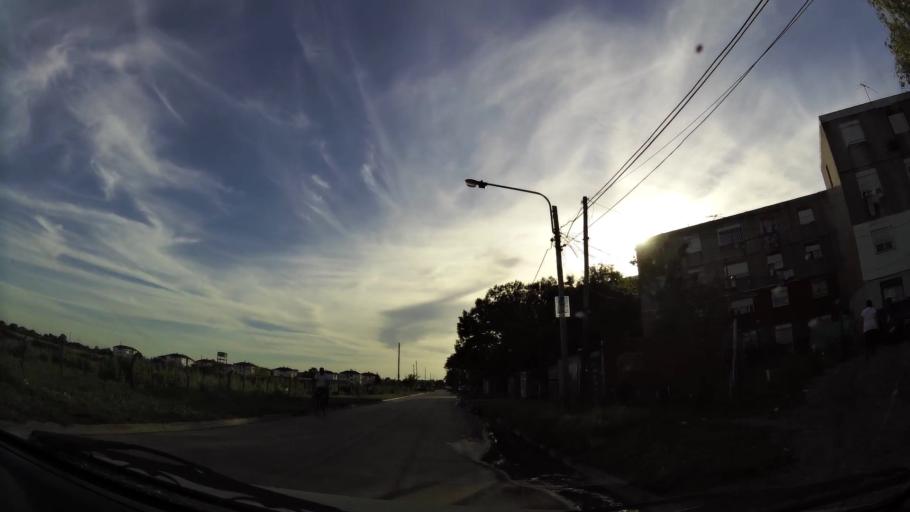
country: AR
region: Buenos Aires
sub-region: Partido de Almirante Brown
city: Adrogue
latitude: -34.8188
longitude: -58.3364
